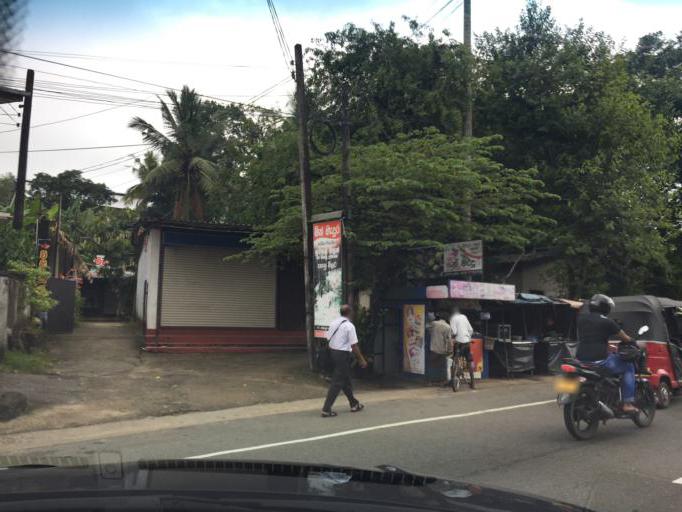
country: LK
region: Western
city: Horana South
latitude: 6.7178
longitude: 80.0673
